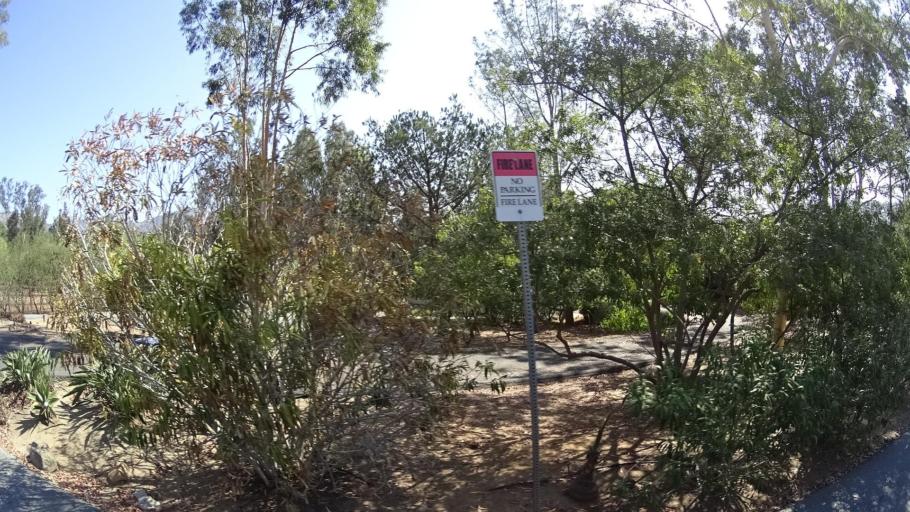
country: US
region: California
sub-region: San Diego County
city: Rancho Santa Fe
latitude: 33.0326
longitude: -117.1659
